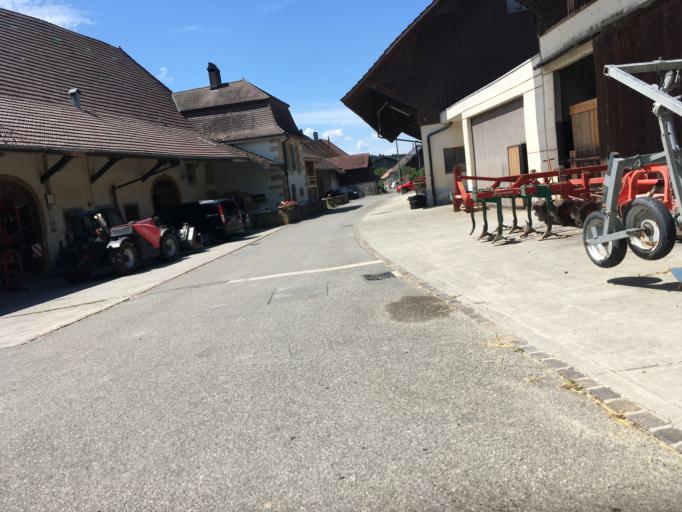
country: CH
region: Neuchatel
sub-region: Neuchatel District
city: Saint-Blaise
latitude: 46.9422
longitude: 6.9995
